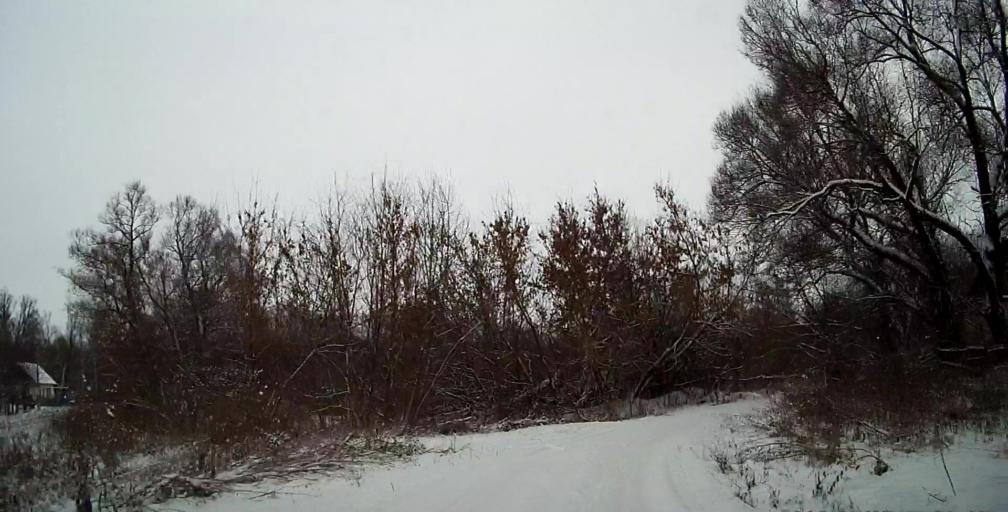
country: RU
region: Lipetsk
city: Lev Tolstoy
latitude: 53.3374
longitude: 39.5846
